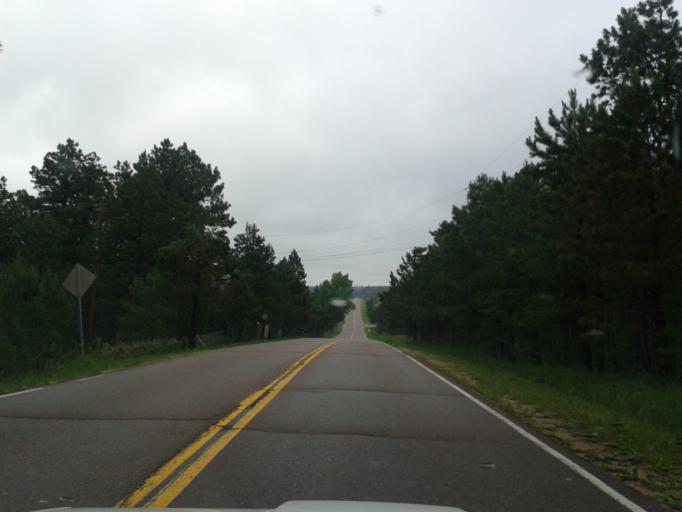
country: US
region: Colorado
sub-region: El Paso County
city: Black Forest
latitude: 39.0453
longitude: -104.6819
